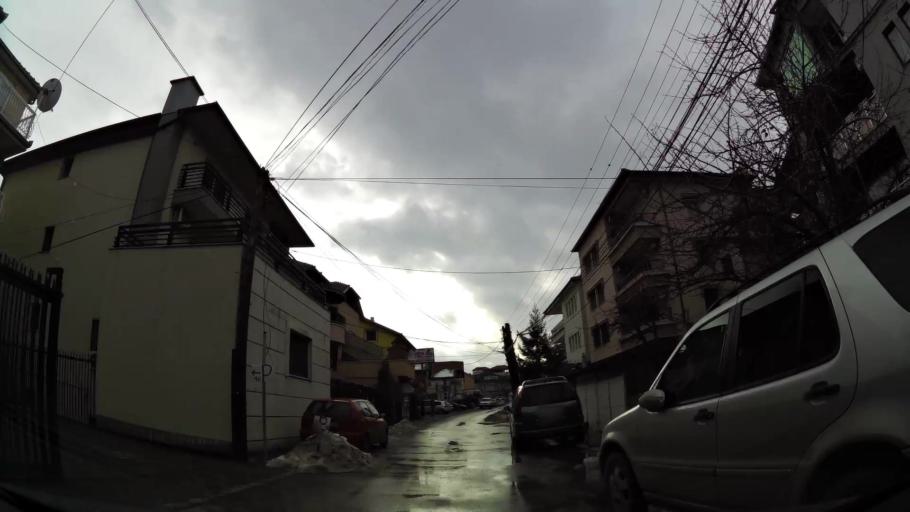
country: XK
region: Pristina
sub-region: Komuna e Prishtines
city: Pristina
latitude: 42.6686
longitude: 21.1542
